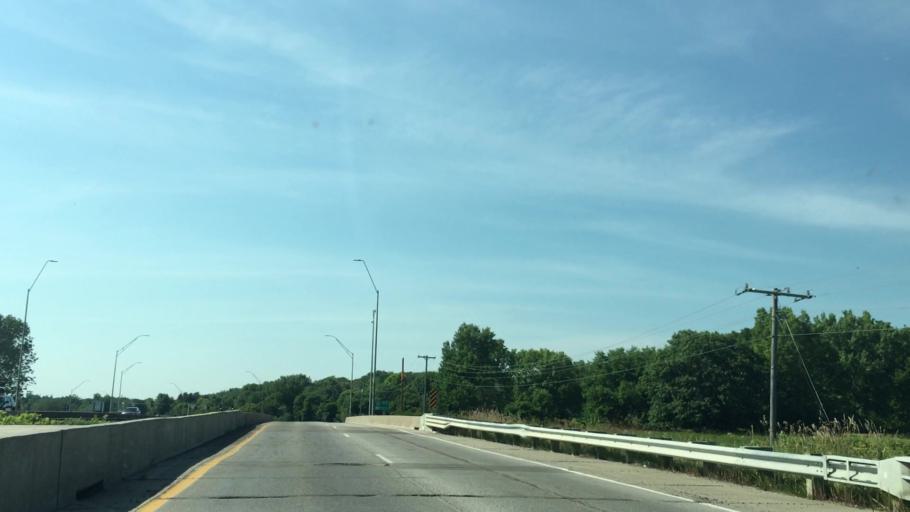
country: US
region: Iowa
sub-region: Johnson County
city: Iowa City
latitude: 41.6860
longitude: -91.5392
